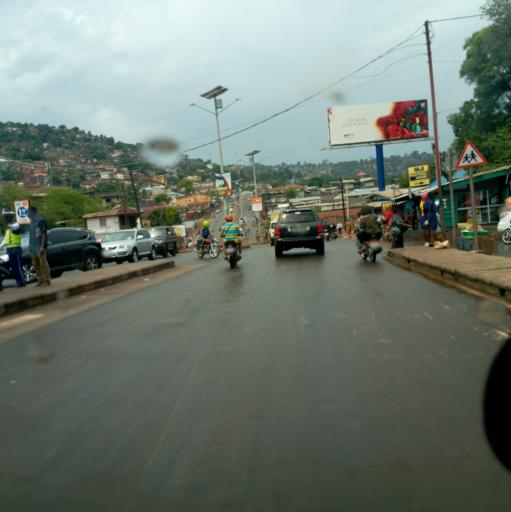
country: SL
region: Western Area
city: Freetown
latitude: 8.4729
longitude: -13.2370
